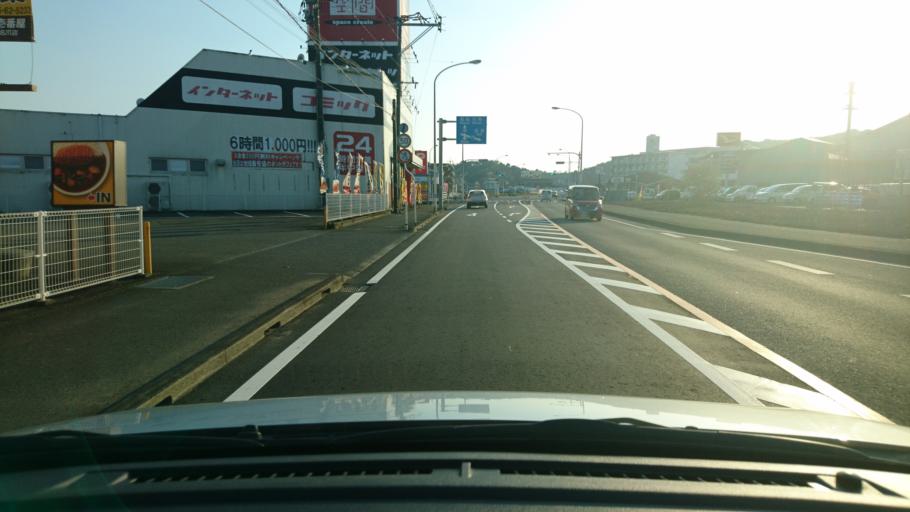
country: JP
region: Miyazaki
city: Miyazaki-shi
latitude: 31.9777
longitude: 131.4442
